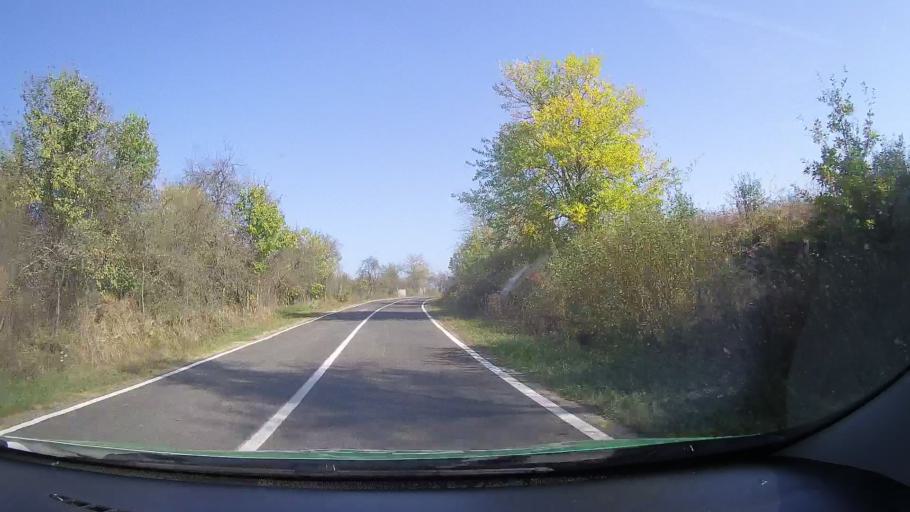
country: RO
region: Timis
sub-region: Comuna Curtea
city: Curtea
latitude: 45.8449
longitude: 22.3126
